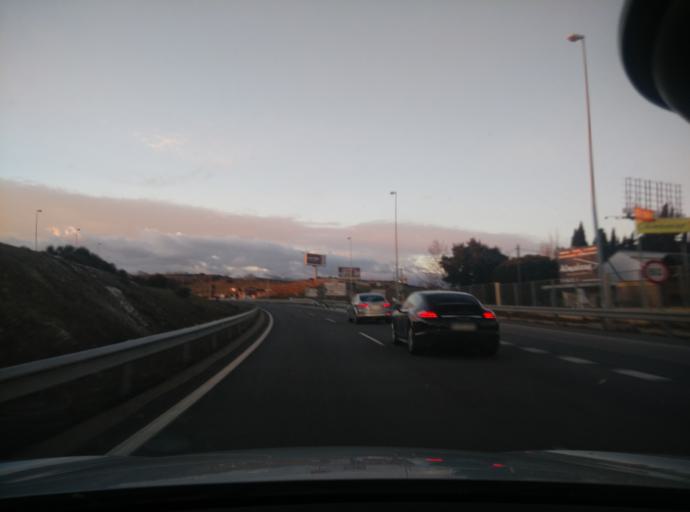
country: ES
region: Madrid
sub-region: Provincia de Madrid
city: Colmenar Viejo
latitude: 40.6496
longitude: -3.7353
